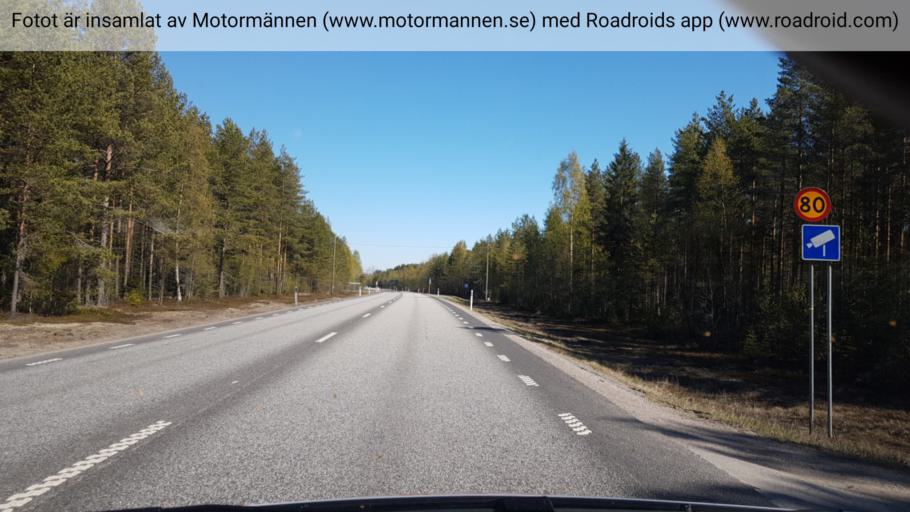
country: SE
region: Vaesterbotten
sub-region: Umea Kommun
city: Roback
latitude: 63.8497
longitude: 20.1209
